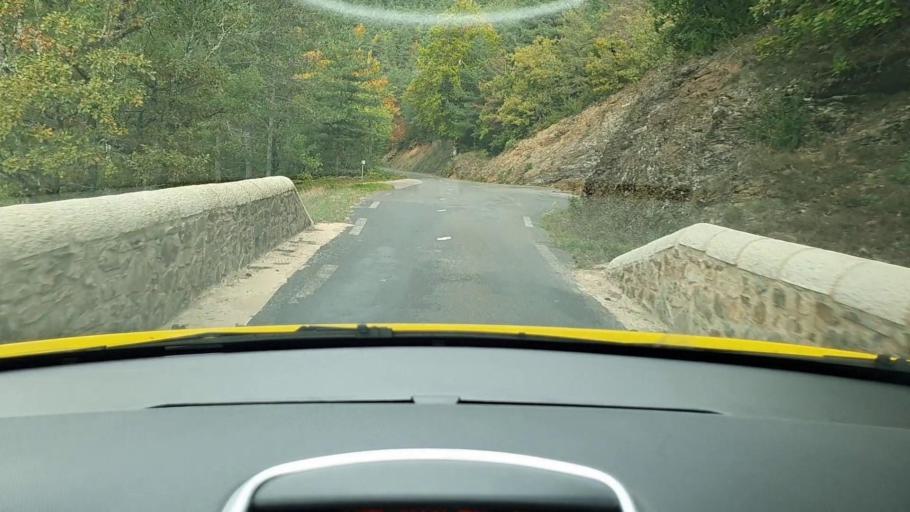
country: FR
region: Languedoc-Roussillon
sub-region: Departement de la Lozere
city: Meyrueis
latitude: 44.1131
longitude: 3.4269
